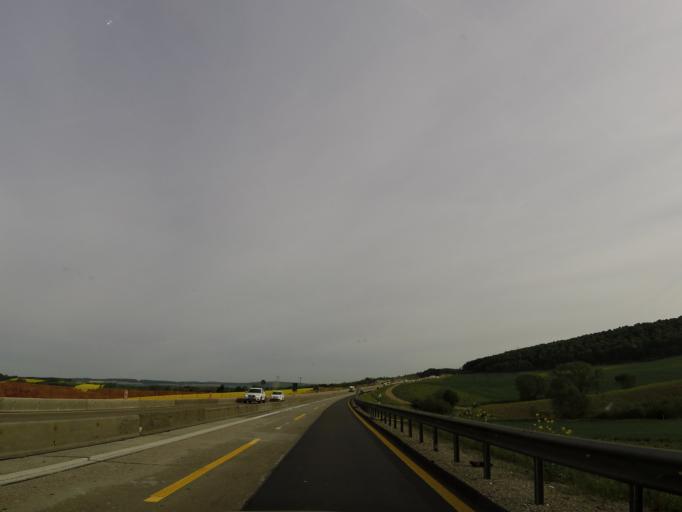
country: DE
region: Lower Saxony
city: Bockenem
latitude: 51.9563
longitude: 10.1403
